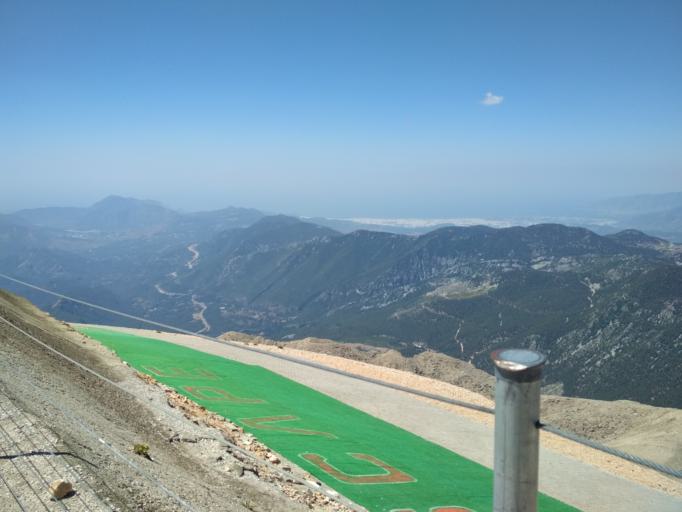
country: TR
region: Antalya
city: Tekirova
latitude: 36.5363
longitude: 30.4418
